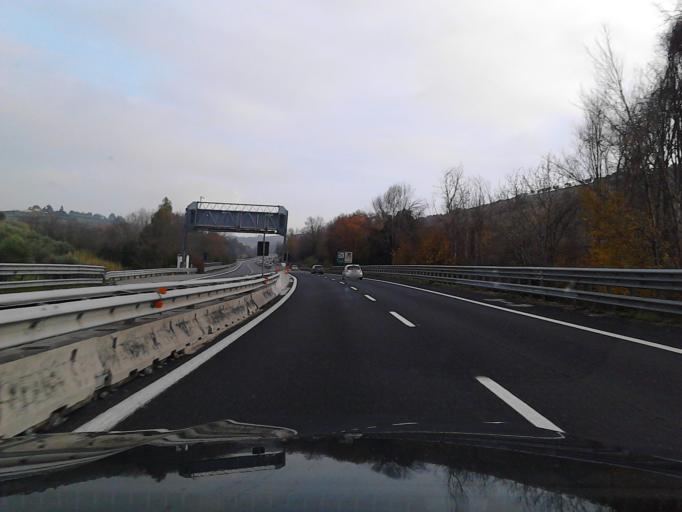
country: IT
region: Abruzzo
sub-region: Provincia di Teramo
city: Colleranesco
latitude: 42.6980
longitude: 13.9190
